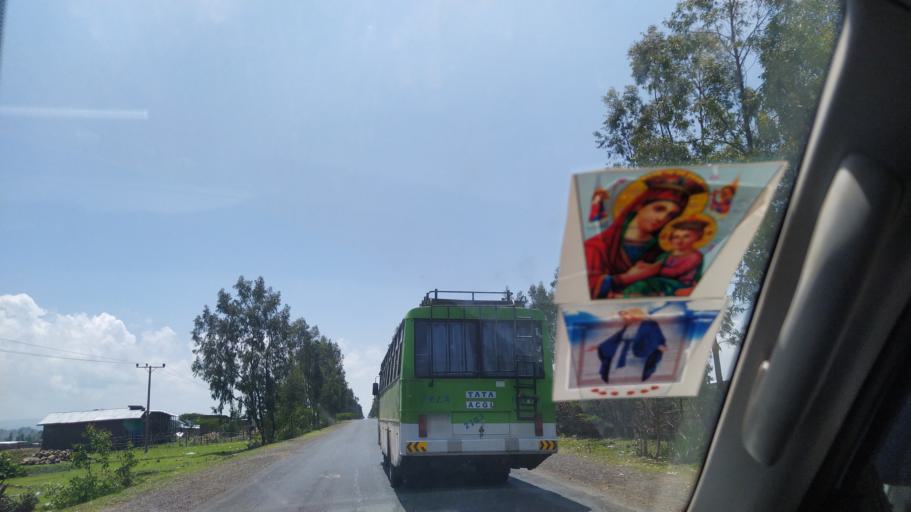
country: ET
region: Southern Nations, Nationalities, and People's Region
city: Butajira
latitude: 7.7864
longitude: 38.1435
